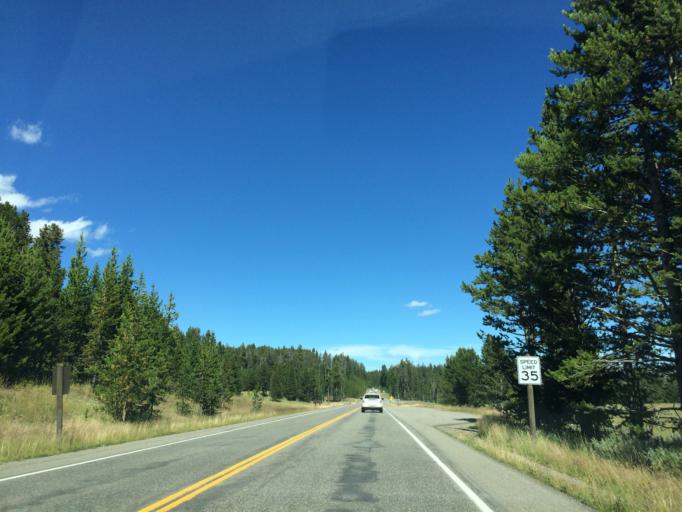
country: US
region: Montana
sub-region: Gallatin County
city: West Yellowstone
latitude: 44.5650
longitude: -110.3907
